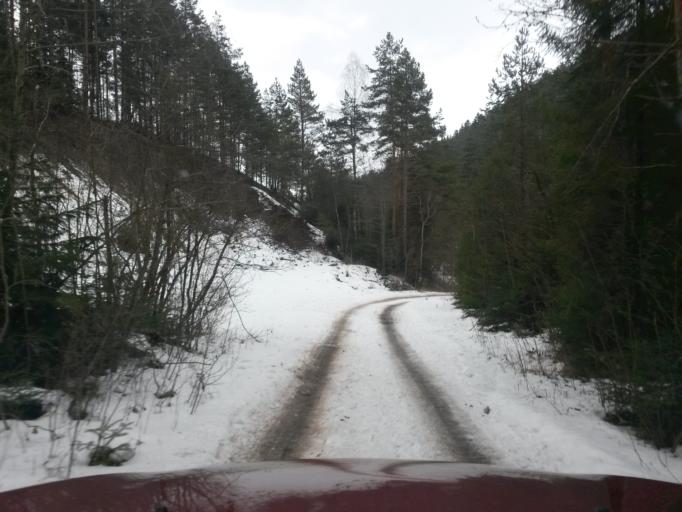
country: SK
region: Kosicky
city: Spisska Nova Ves
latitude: 48.8737
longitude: 20.5815
